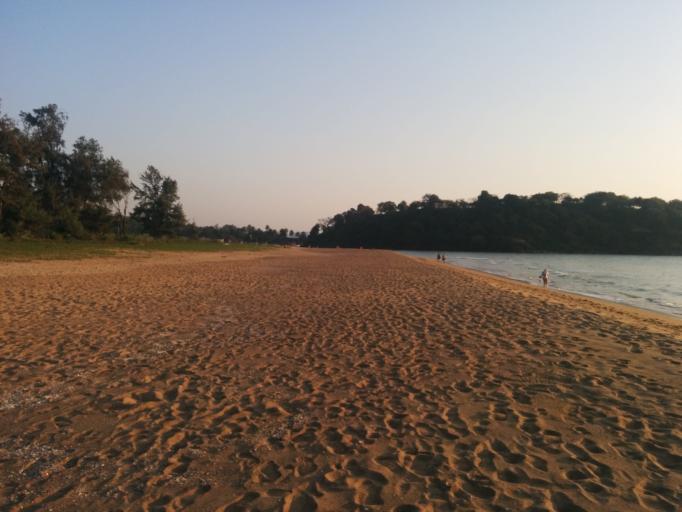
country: IN
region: Karnataka
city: Canacona
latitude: 14.9879
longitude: 74.0377
